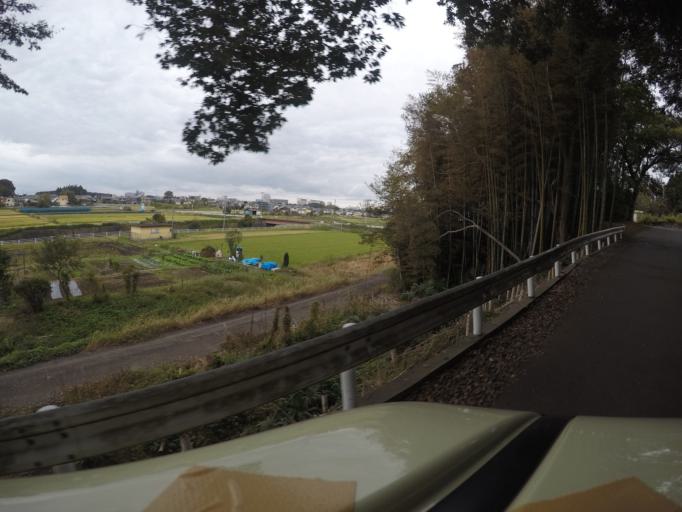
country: JP
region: Ibaraki
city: Naka
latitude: 36.0771
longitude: 140.1349
